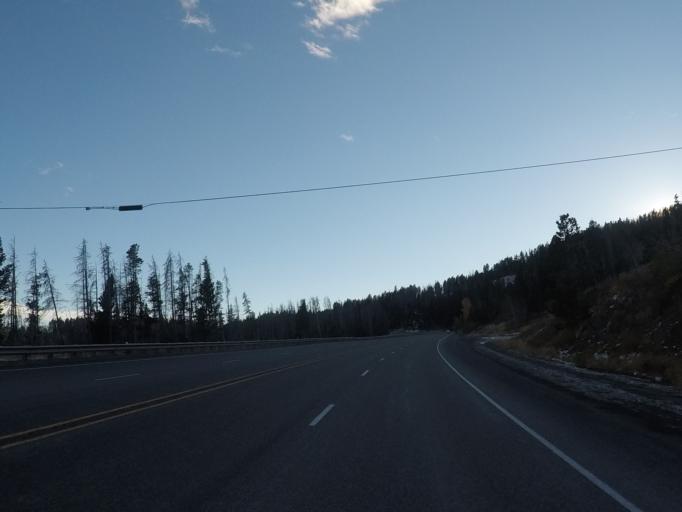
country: US
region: Montana
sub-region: Lewis and Clark County
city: Helena West Side
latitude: 46.5708
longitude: -112.3018
